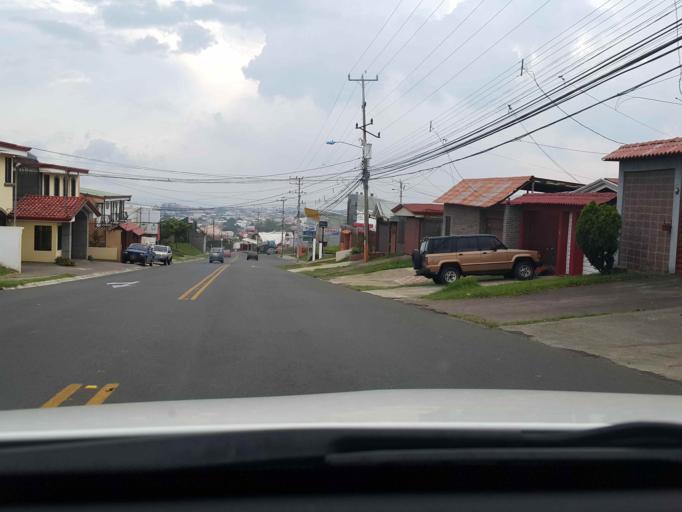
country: CR
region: Heredia
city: San Pablo
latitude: 10.0004
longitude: -84.1026
